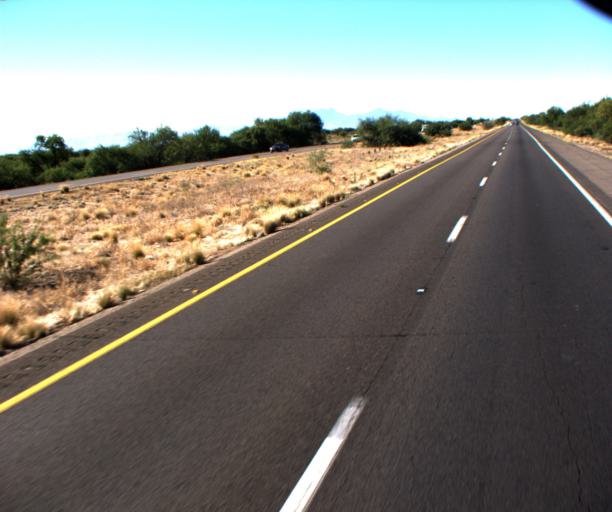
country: US
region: Arizona
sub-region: Pima County
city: Summit
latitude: 32.0989
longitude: -110.9936
